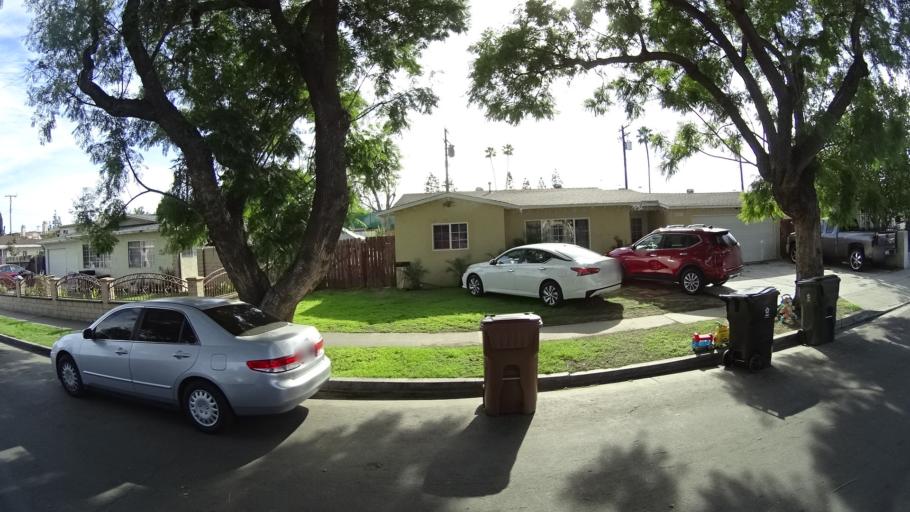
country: US
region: California
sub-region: Orange County
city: Garden Grove
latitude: 33.7610
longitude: -117.9086
